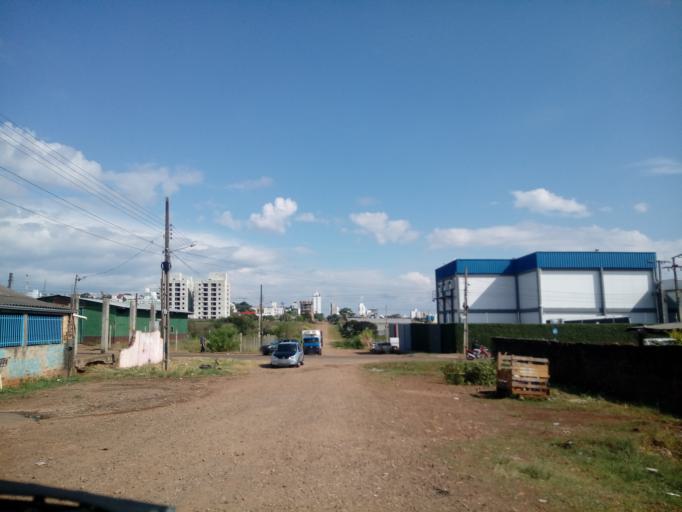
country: BR
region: Santa Catarina
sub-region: Chapeco
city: Chapeco
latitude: -27.0982
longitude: -52.5934
